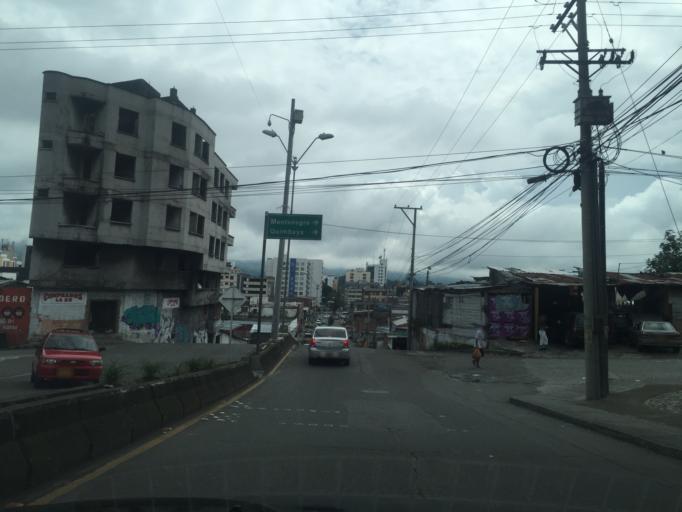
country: CO
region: Quindio
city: Armenia
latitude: 4.5355
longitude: -75.6779
